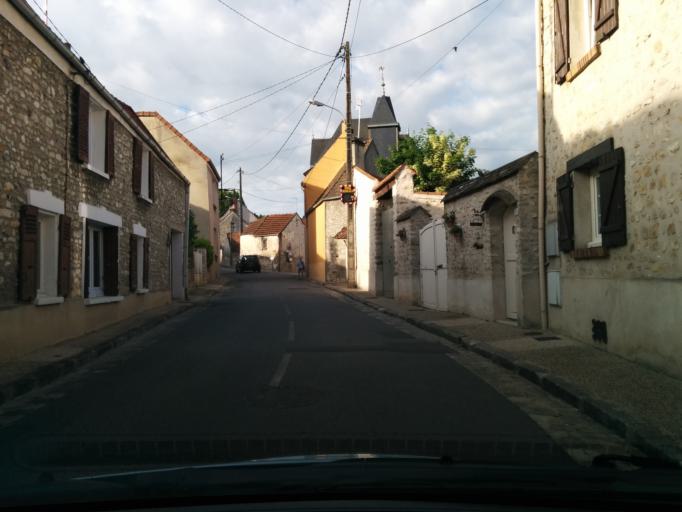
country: FR
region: Ile-de-France
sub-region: Departement des Yvelines
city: Follainville-Dennemont
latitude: 49.0417
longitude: 1.6885
